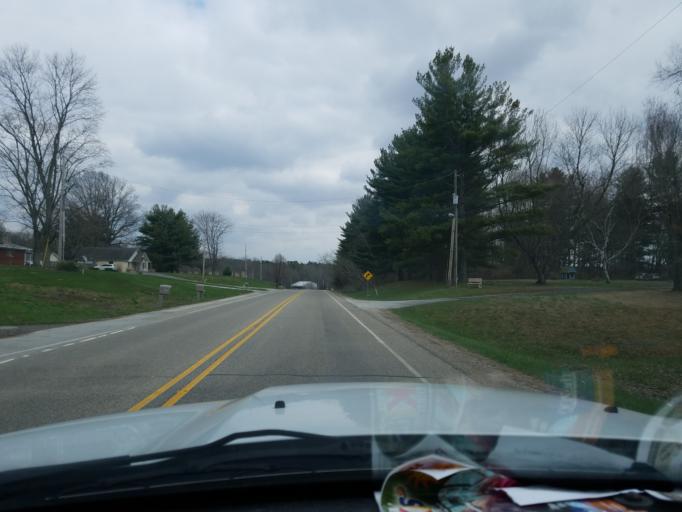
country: US
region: Indiana
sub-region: Vigo County
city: Seelyville
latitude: 39.4080
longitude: -87.3271
